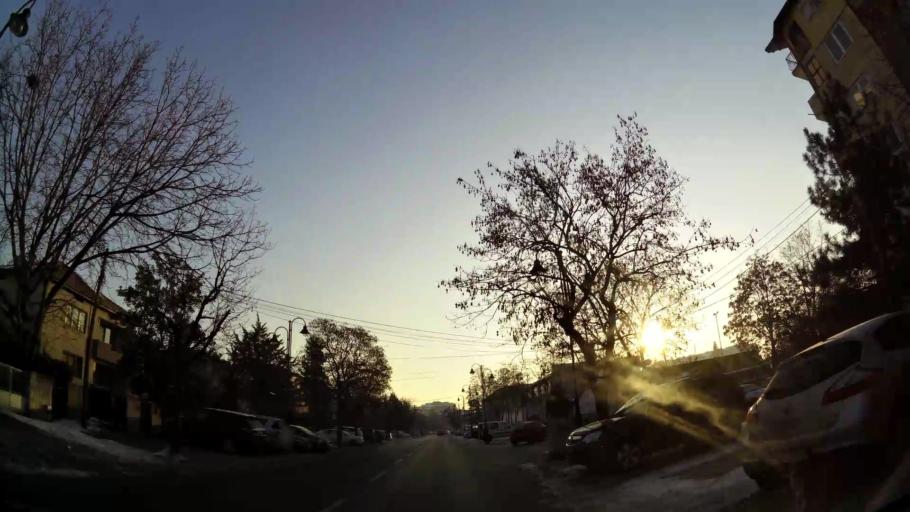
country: MK
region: Karpos
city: Skopje
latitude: 42.0051
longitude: 21.4117
